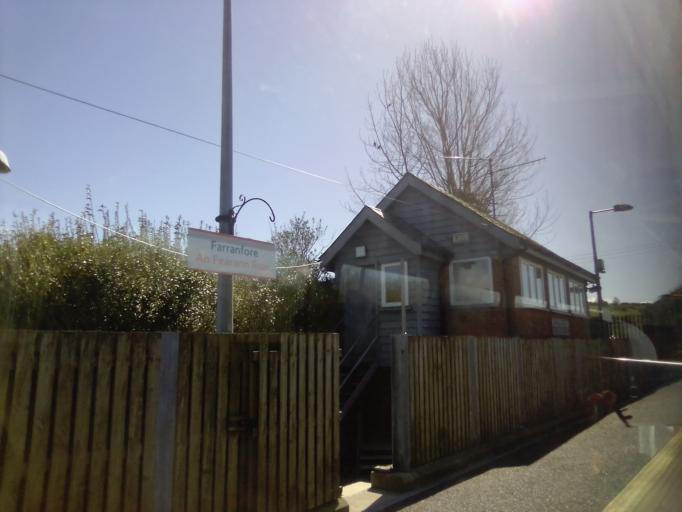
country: IE
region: Munster
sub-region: Ciarrai
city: Castleisland
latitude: 52.1736
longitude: -9.5528
